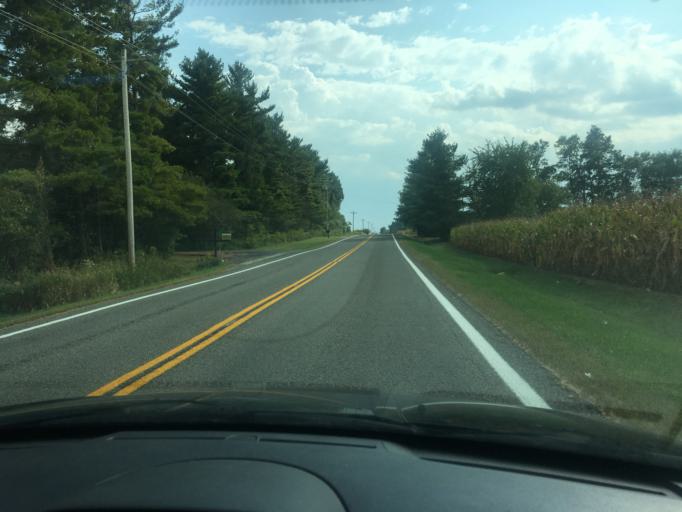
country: US
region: Ohio
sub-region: Champaign County
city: Urbana
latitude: 40.1398
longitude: -83.8347
